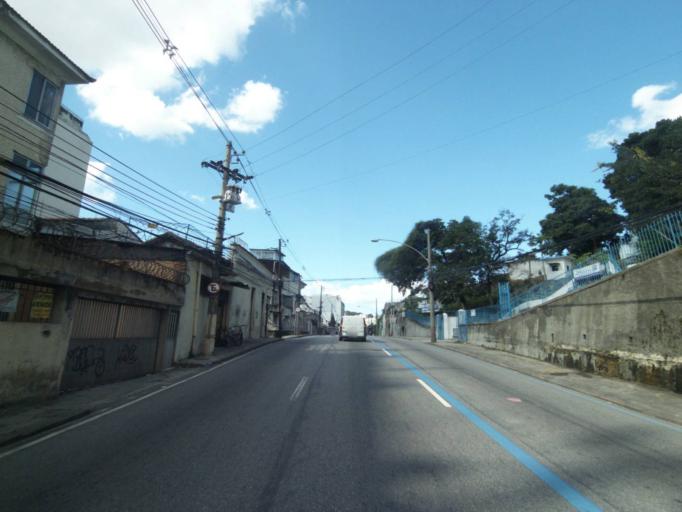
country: BR
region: Rio de Janeiro
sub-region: Rio De Janeiro
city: Rio de Janeiro
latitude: -22.9029
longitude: -43.2480
